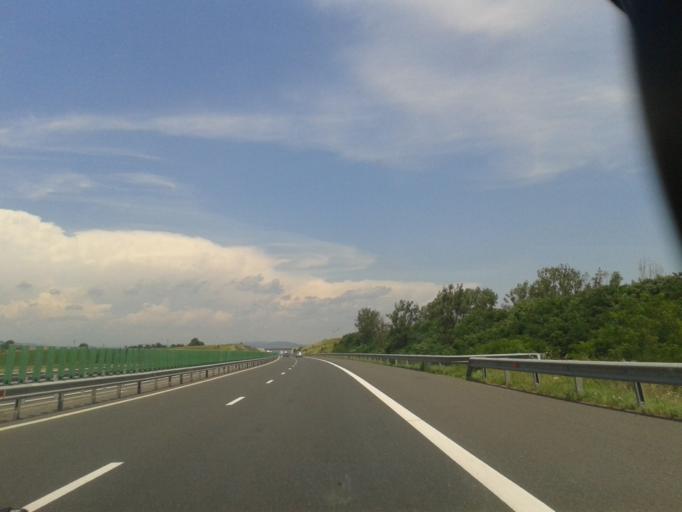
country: RO
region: Hunedoara
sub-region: Comuna Turdas
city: Turdas
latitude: 45.8419
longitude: 23.1245
